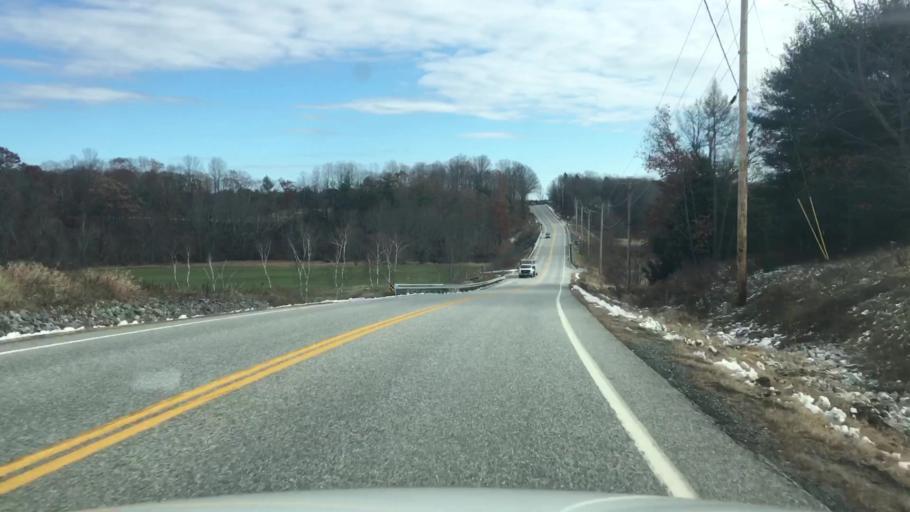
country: US
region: Maine
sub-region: Androscoggin County
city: Leeds
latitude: 44.3458
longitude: -70.1540
